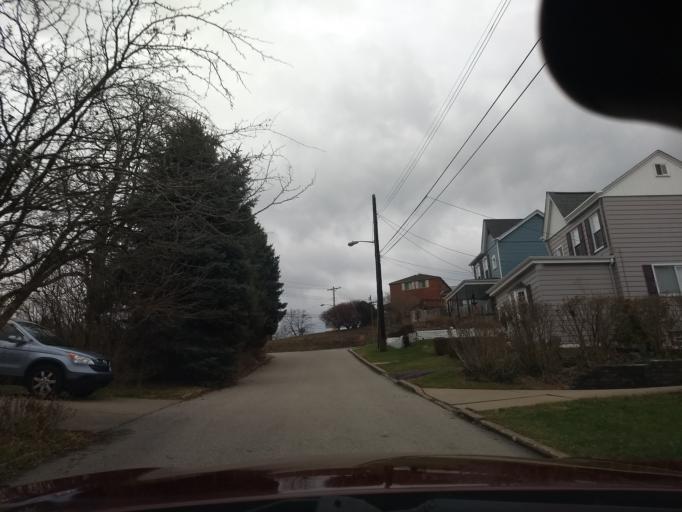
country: US
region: Pennsylvania
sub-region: Allegheny County
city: Homestead
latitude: 40.4191
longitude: -79.9422
